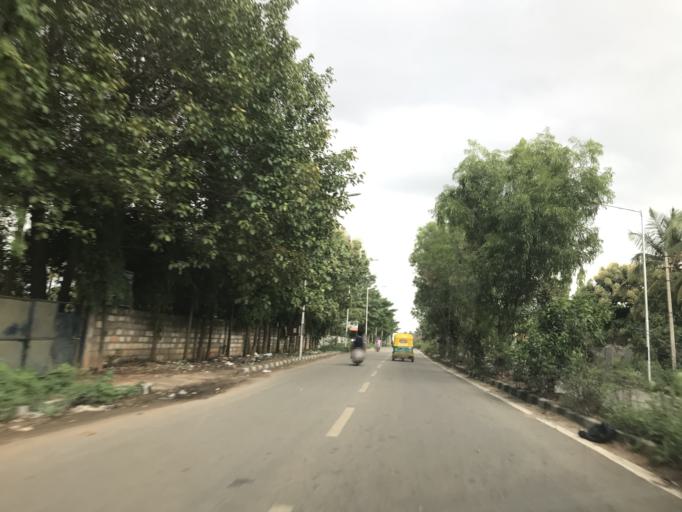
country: IN
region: Karnataka
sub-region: Bangalore Urban
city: Yelahanka
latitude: 13.1227
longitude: 77.6345
